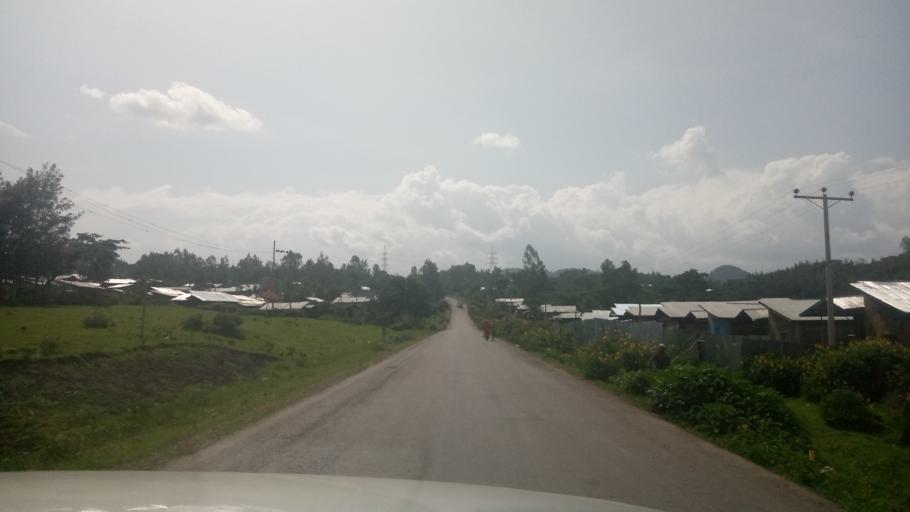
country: ET
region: Oromiya
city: Agaro
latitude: 7.9978
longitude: 36.5000
